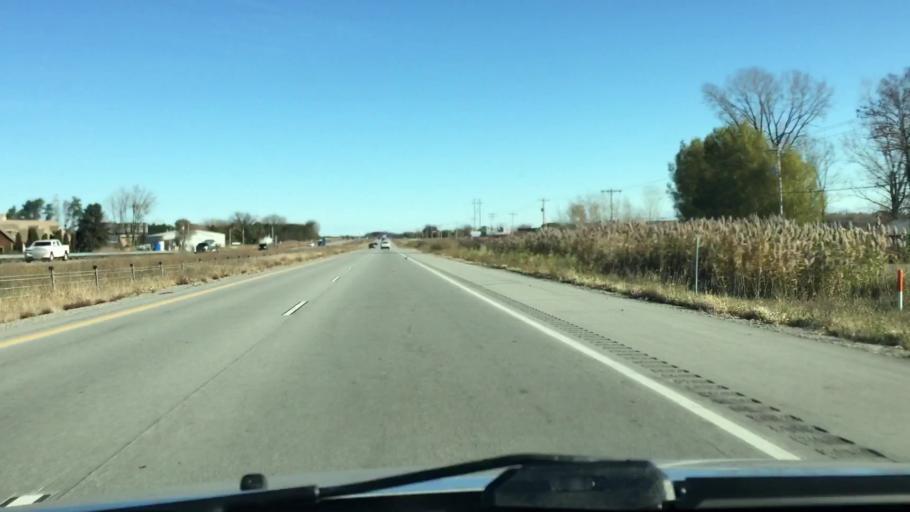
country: US
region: Wisconsin
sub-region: Brown County
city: Wrightstown
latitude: 44.3718
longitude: -88.1730
